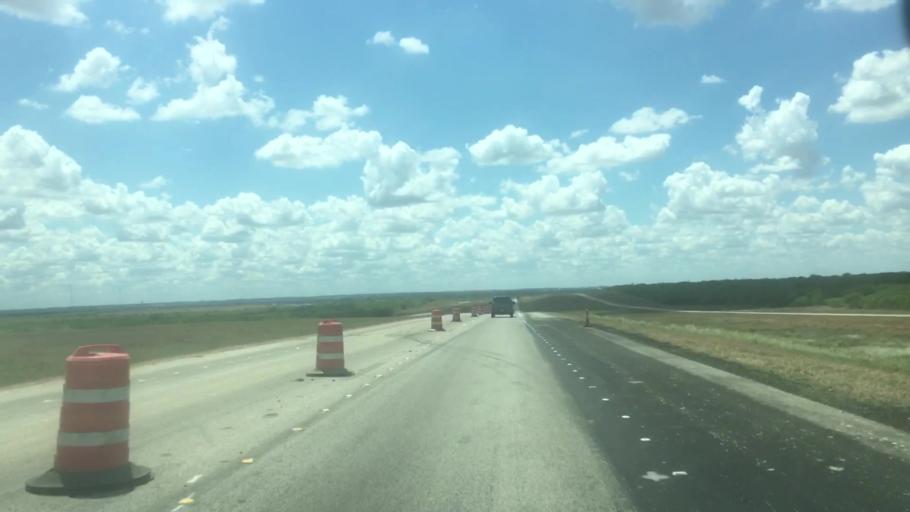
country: US
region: Texas
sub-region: Caldwell County
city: Martindale
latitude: 29.8128
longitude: -97.7650
